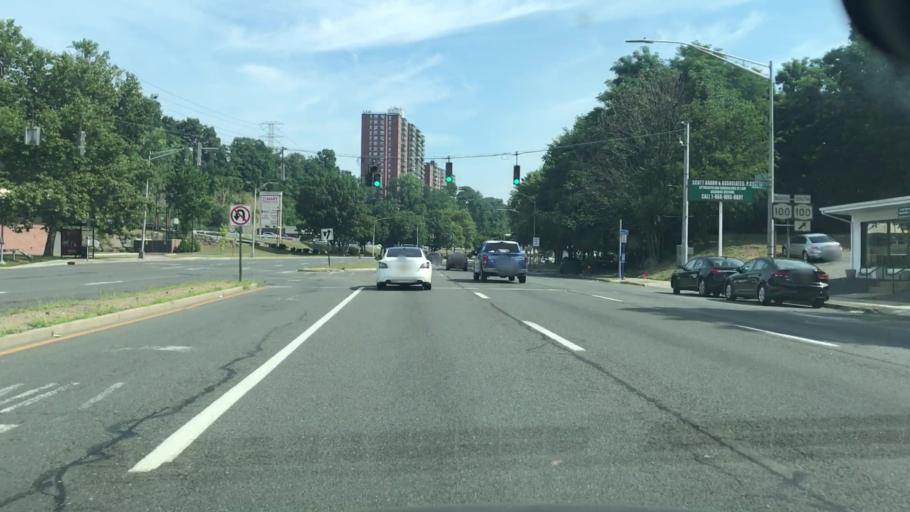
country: US
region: New York
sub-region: Westchester County
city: Tuckahoe
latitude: 40.9583
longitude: -73.8417
